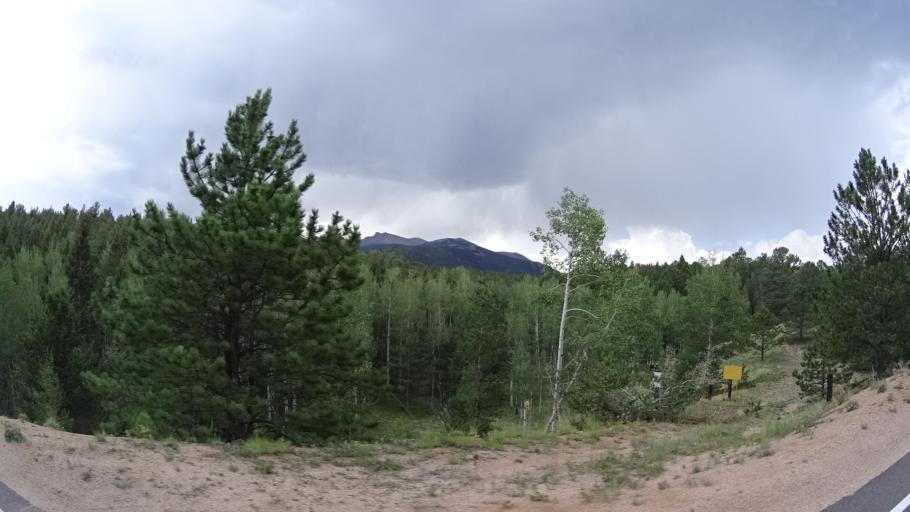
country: US
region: Colorado
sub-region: El Paso County
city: Cascade-Chipita Park
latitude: 38.9128
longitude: -105.0304
